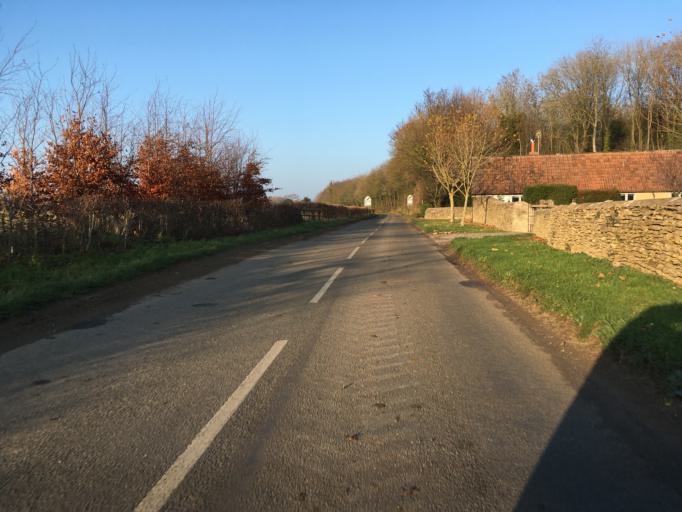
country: GB
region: England
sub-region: Wiltshire
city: Luckington
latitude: 51.5582
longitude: -2.2885
